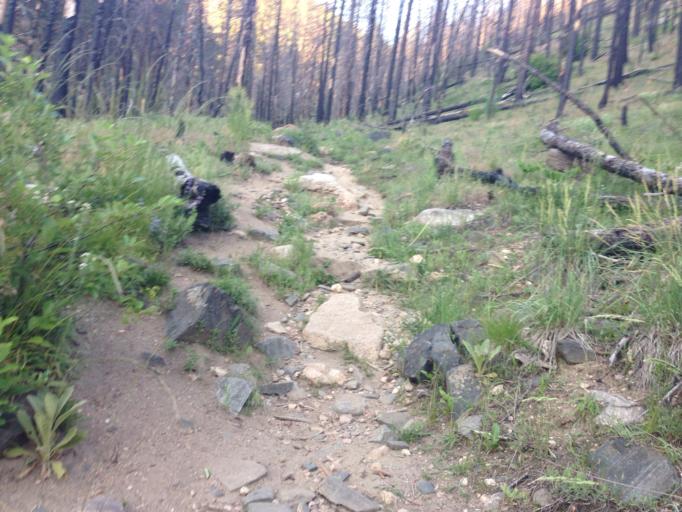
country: US
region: Colorado
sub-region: Larimer County
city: Laporte
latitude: 40.7053
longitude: -105.2964
